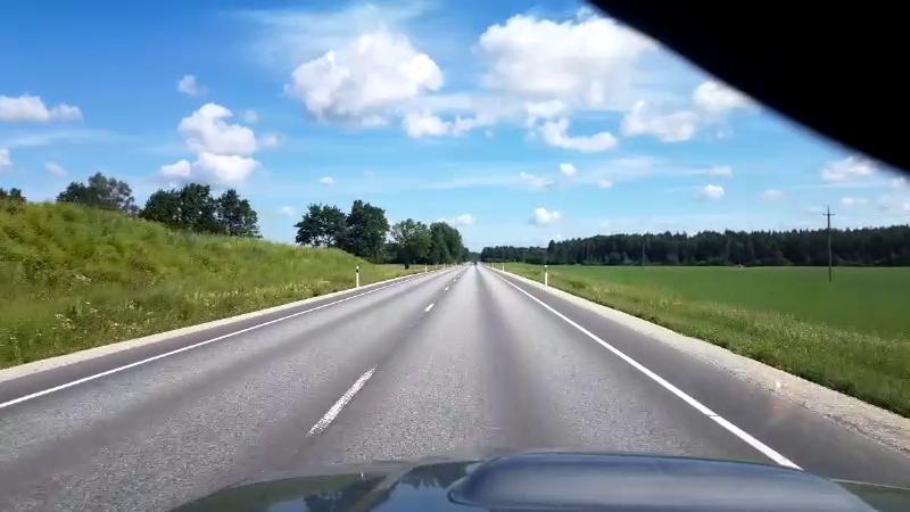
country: EE
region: Jaervamaa
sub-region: Paide linn
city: Paide
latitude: 58.9880
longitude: 25.6709
